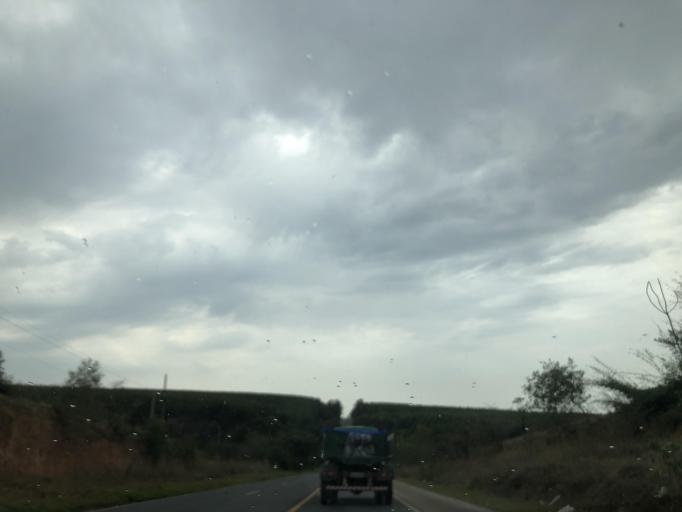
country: BR
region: Sao Paulo
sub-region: Salto De Pirapora
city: Salto de Pirapora
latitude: -23.6810
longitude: -47.6051
